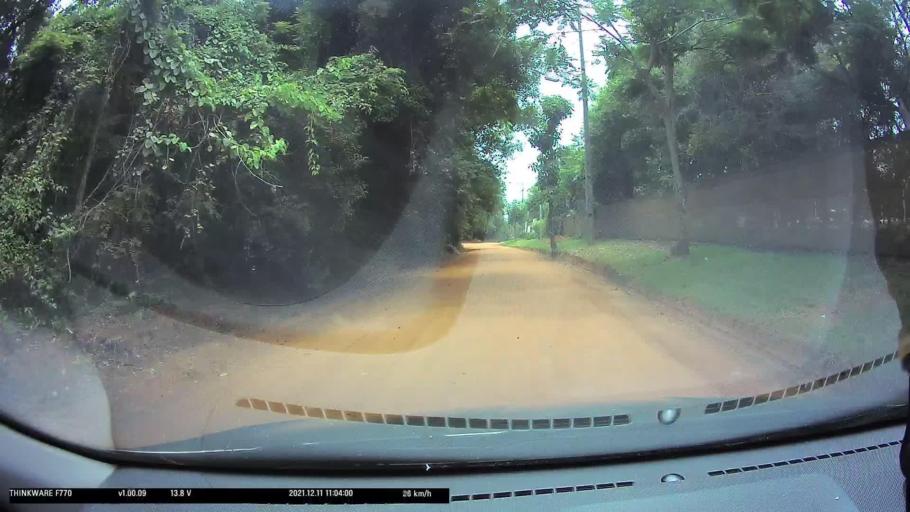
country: PY
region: Cordillera
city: Altos
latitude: -25.3023
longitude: -57.2425
